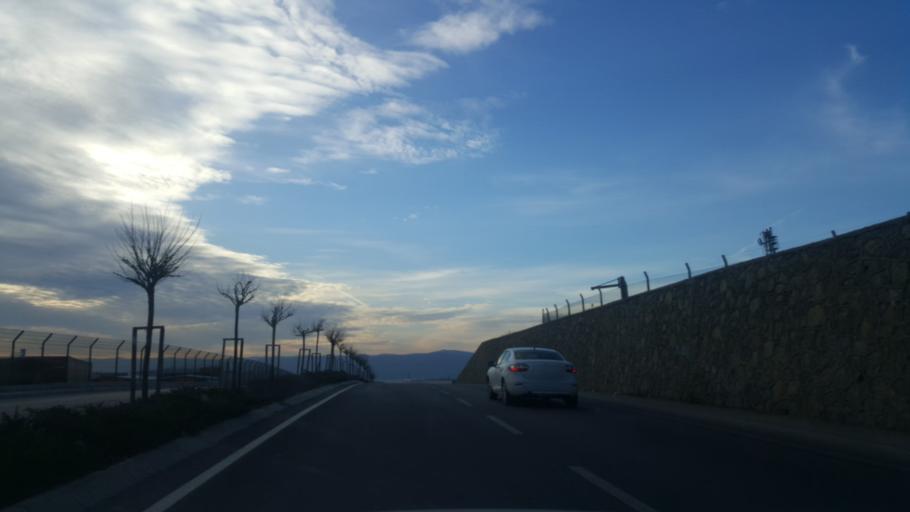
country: TR
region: Kocaeli
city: Tavsanli
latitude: 40.8222
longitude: 29.5594
